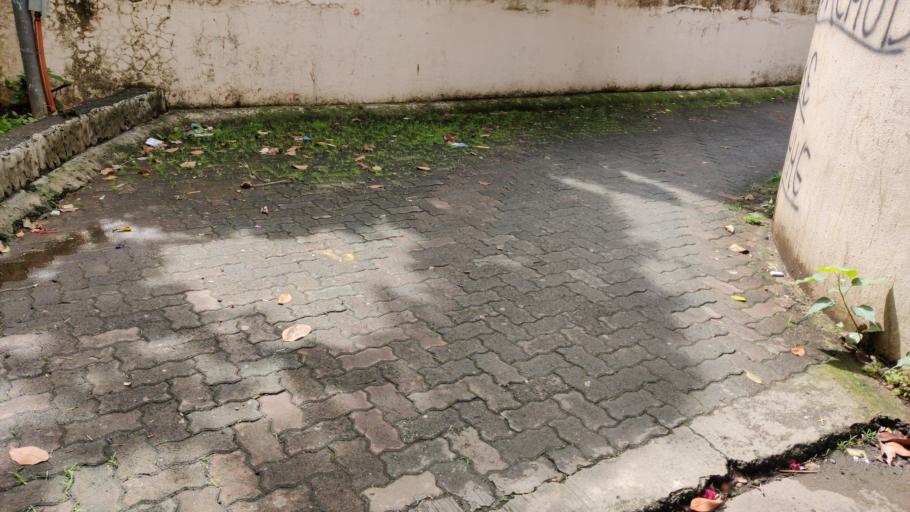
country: IN
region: Maharashtra
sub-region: Mumbai Suburban
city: Borivli
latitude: 19.2479
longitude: 72.8603
